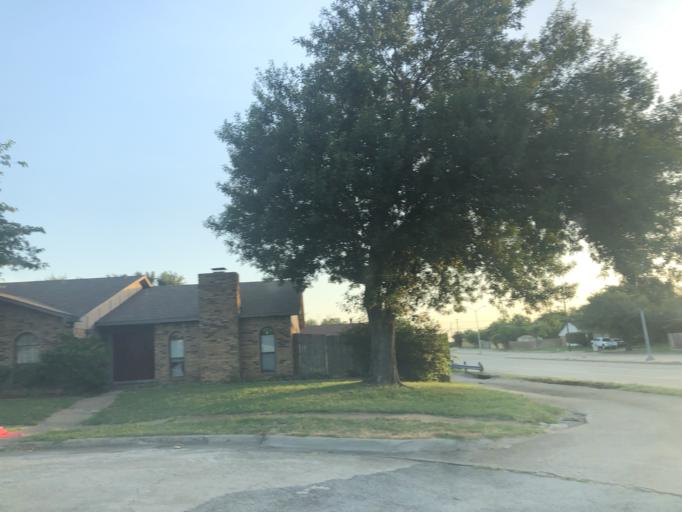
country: US
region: Texas
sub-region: Dallas County
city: Duncanville
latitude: 32.6437
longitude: -96.9530
